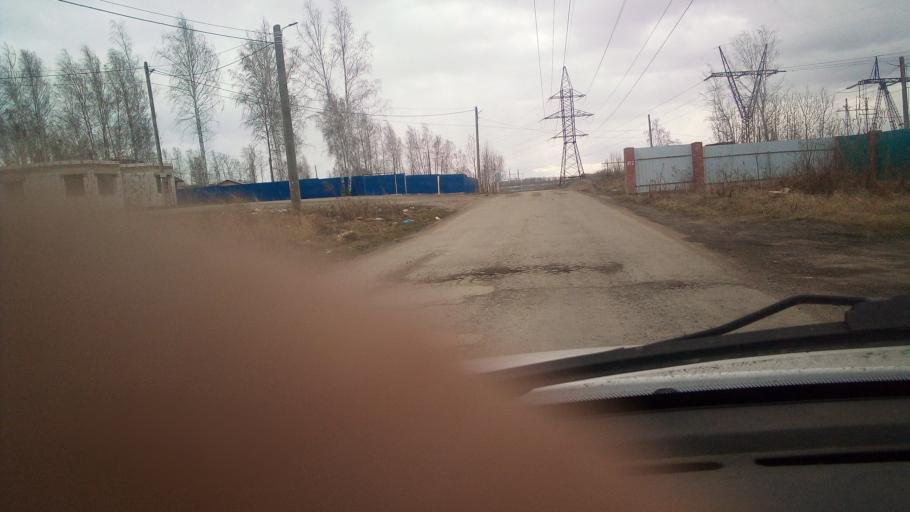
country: RU
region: Chelyabinsk
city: Sargazy
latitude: 55.1291
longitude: 61.2410
